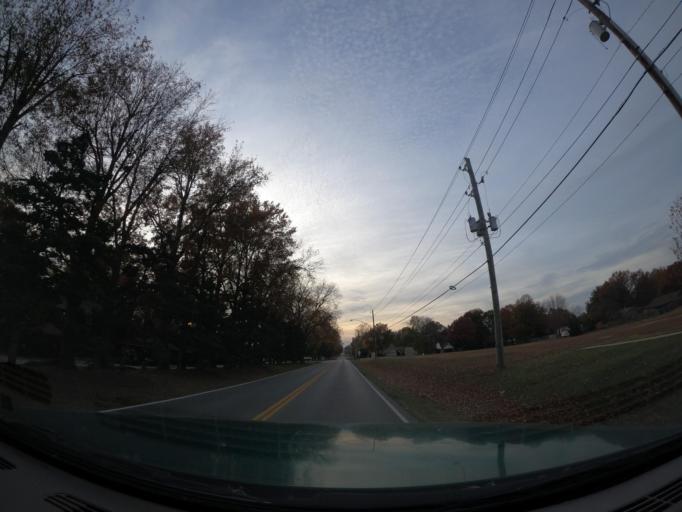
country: US
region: Oklahoma
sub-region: Tulsa County
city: Broken Arrow
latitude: 35.9738
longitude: -95.7994
